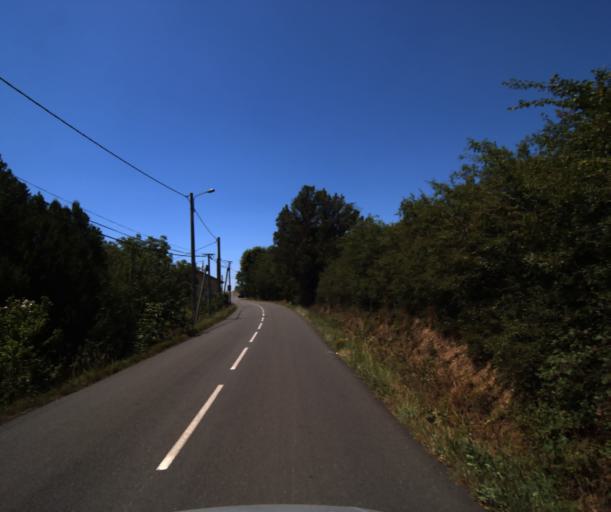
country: FR
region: Midi-Pyrenees
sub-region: Departement de la Haute-Garonne
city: Muret
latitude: 43.4599
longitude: 1.3139
